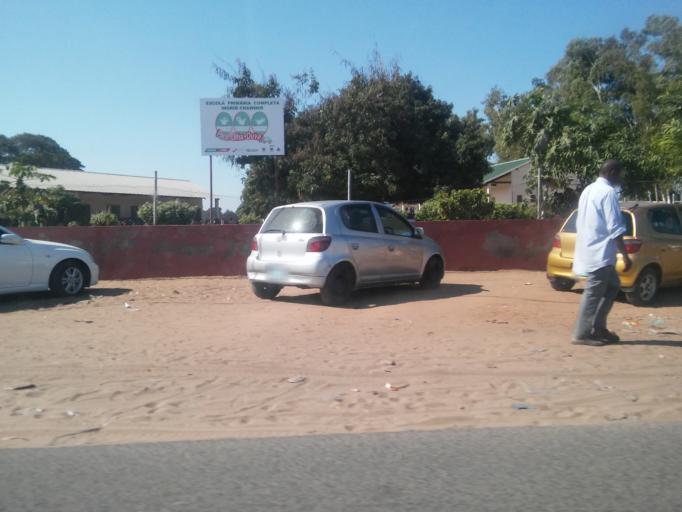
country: MZ
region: Maputo City
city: Maputo
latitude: -25.8587
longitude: 32.5670
